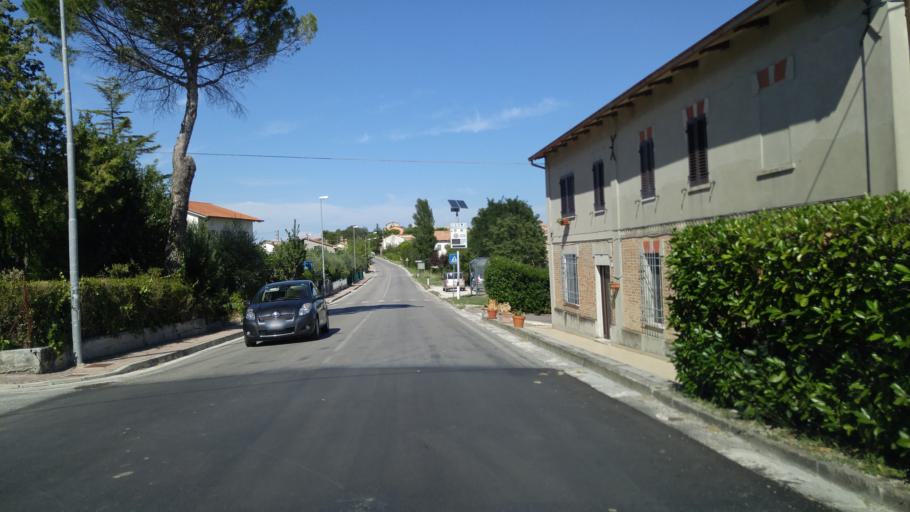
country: IT
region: The Marches
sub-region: Provincia di Pesaro e Urbino
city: Orciano di Pesaro
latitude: 43.7021
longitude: 12.9787
